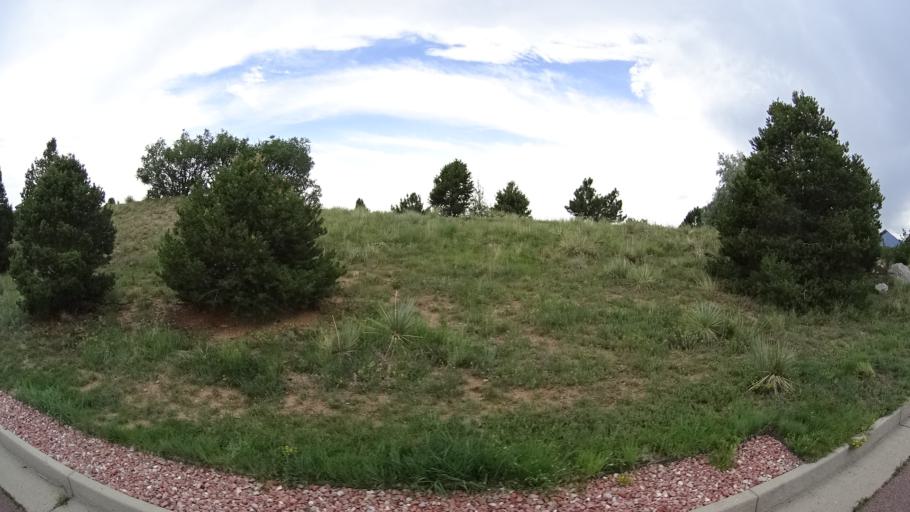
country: US
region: Colorado
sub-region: El Paso County
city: Colorado Springs
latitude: 38.9089
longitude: -104.8344
